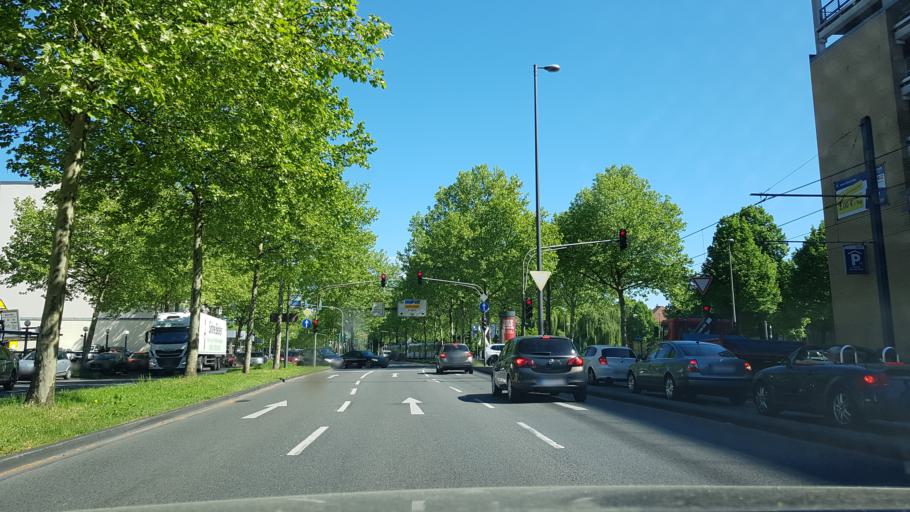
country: DE
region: North Rhine-Westphalia
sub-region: Regierungsbezirk Koln
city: Muelheim
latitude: 50.9634
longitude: 7.0052
